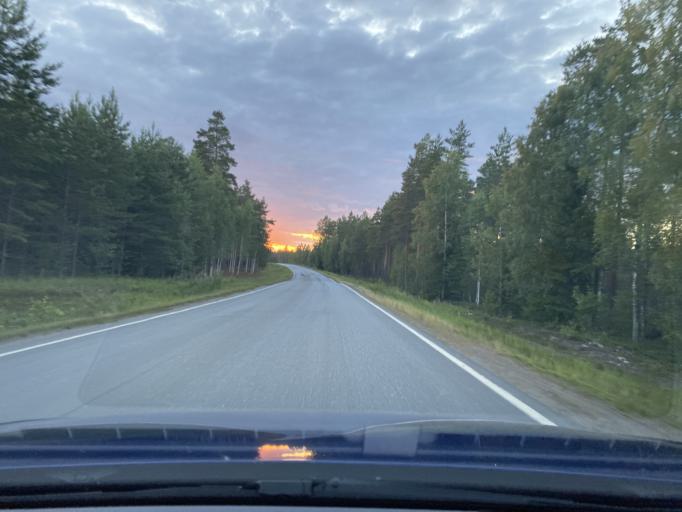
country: FI
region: Haeme
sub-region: Forssa
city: Tammela
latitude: 60.9345
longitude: 23.7888
